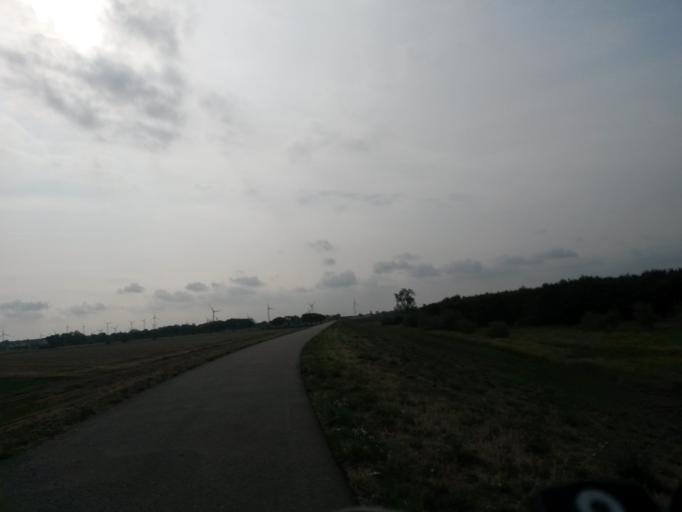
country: DE
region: Saxony-Anhalt
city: Tangermunde
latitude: 52.5504
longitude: 11.9993
